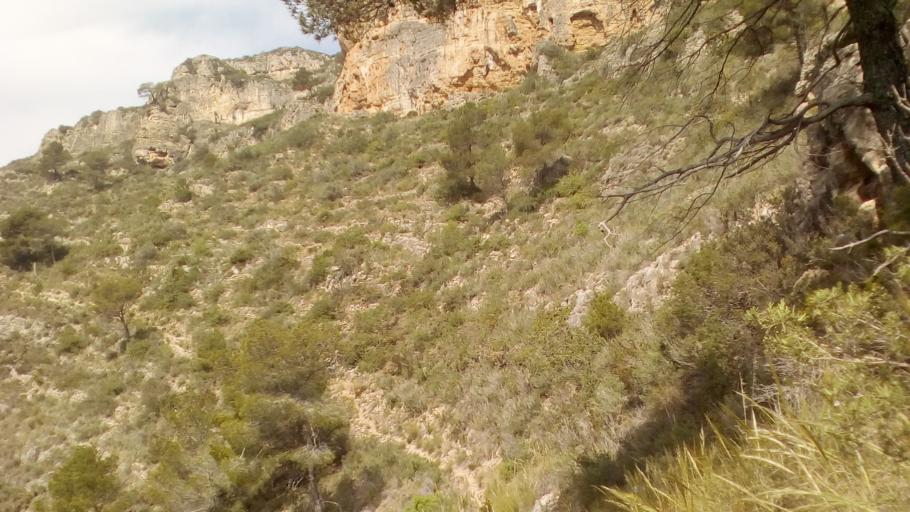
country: ES
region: Valencia
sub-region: Provincia de Valencia
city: Xeraco,Jaraco
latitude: 39.0385
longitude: -0.2388
